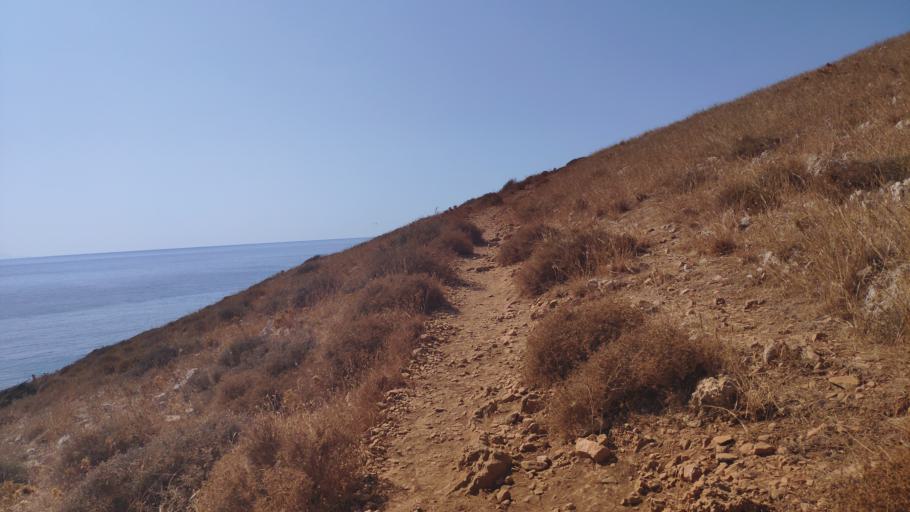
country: GR
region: Peloponnese
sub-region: Nomos Lakonias
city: Gytheio
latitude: 36.3983
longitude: 22.4848
